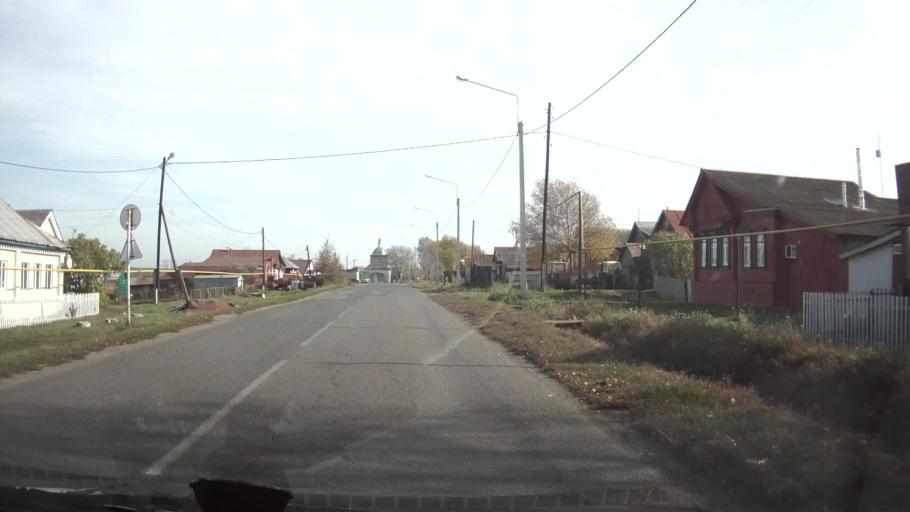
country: RU
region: Mordoviya
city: Turgenevo
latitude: 54.8547
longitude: 46.4048
